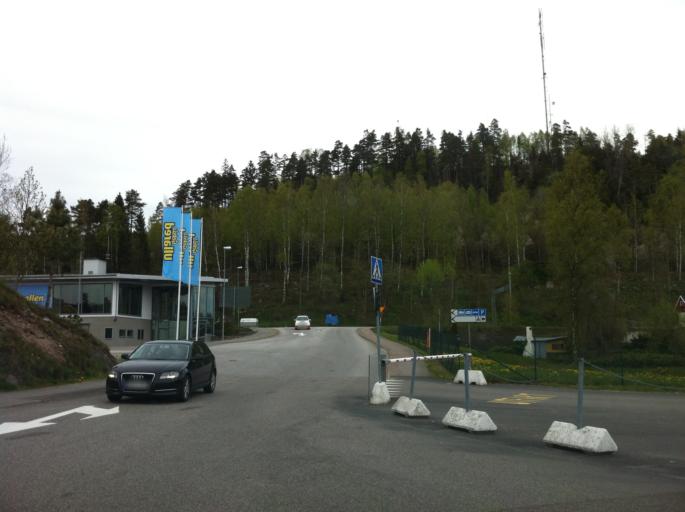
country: SE
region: Halland
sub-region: Falkenbergs Kommun
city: Falkenberg
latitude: 57.1367
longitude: 12.7106
